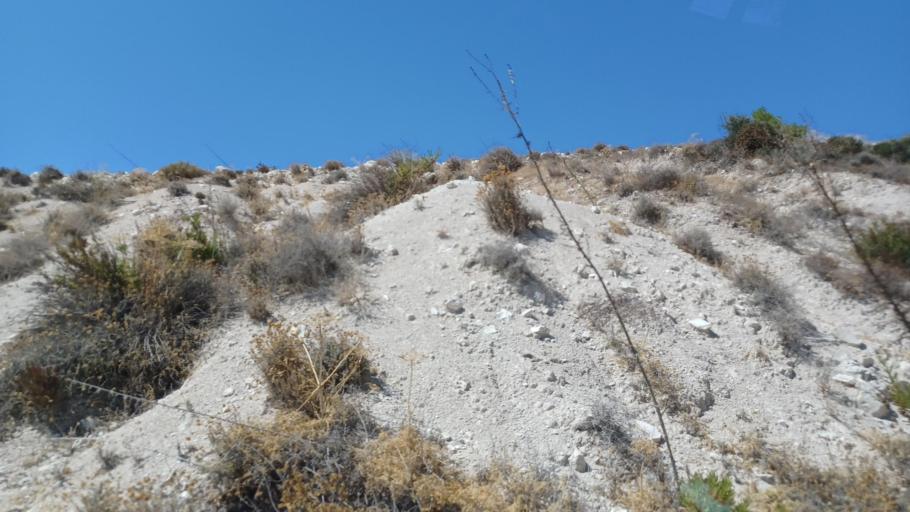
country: CY
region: Larnaka
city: Athienou
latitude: 35.0042
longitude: 33.5543
